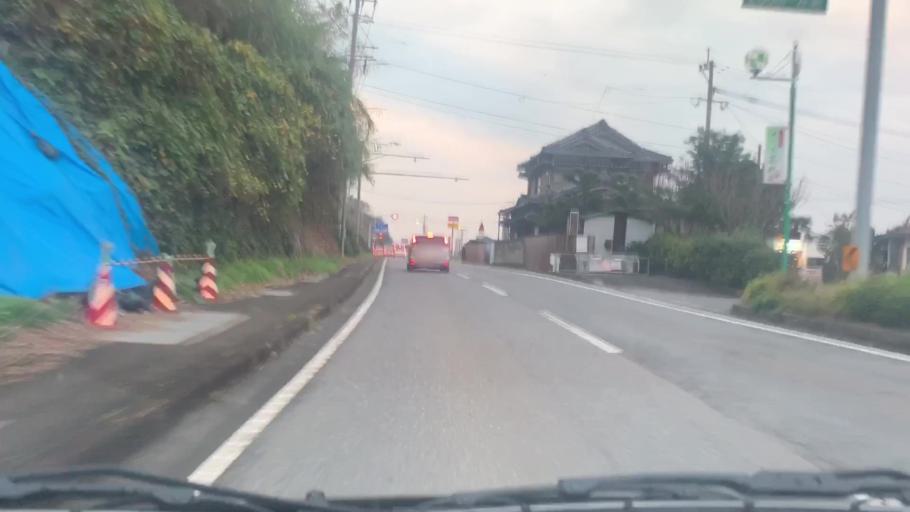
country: JP
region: Saga Prefecture
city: Ureshinomachi-shimojuku
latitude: 33.0376
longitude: 129.9222
